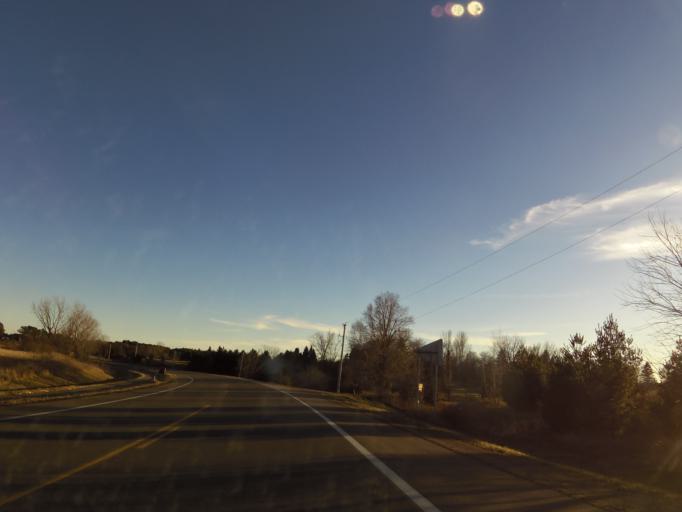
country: US
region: Minnesota
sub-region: Washington County
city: Grant
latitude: 45.1334
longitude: -92.8419
